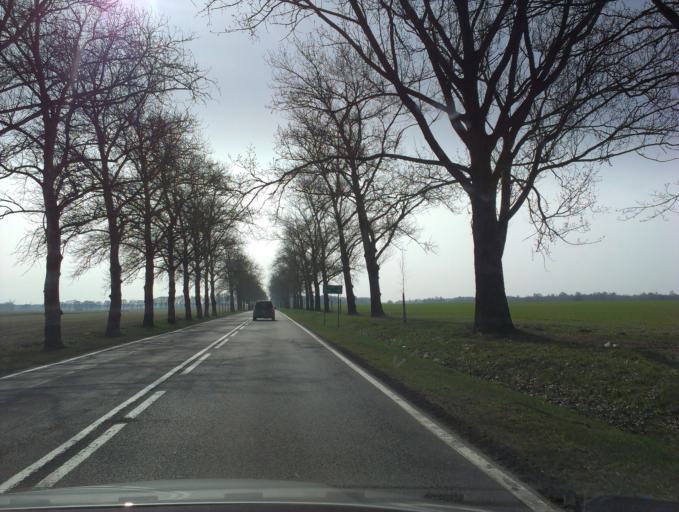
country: PL
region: Greater Poland Voivodeship
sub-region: Powiat zlotowski
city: Okonek
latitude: 53.5987
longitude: 16.8127
